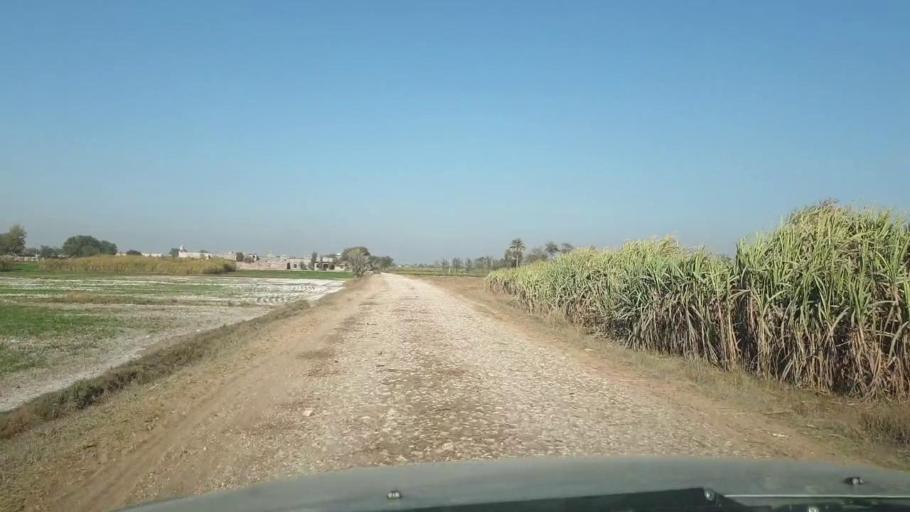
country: PK
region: Sindh
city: Ghotki
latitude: 28.0439
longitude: 69.3352
